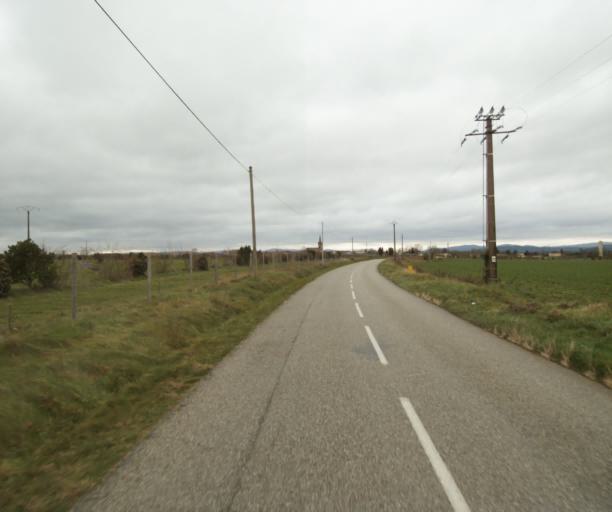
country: FR
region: Midi-Pyrenees
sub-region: Departement de l'Ariege
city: Pamiers
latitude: 43.1605
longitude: 1.6364
